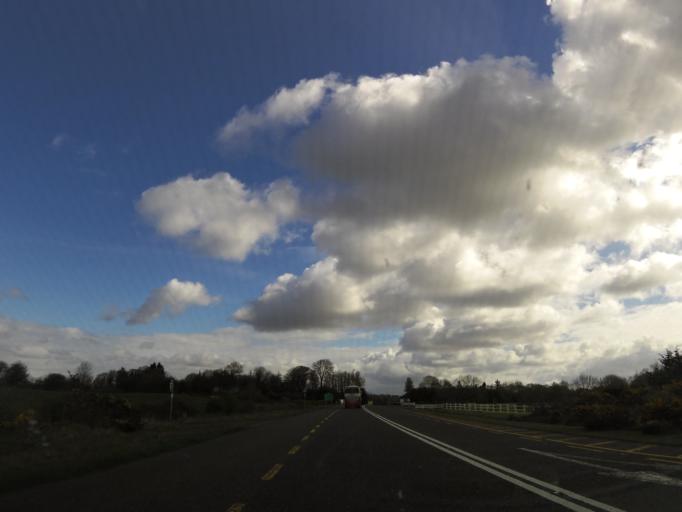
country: IE
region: Connaught
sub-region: Maigh Eo
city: Kiltamagh
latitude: 53.8214
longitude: -8.8894
